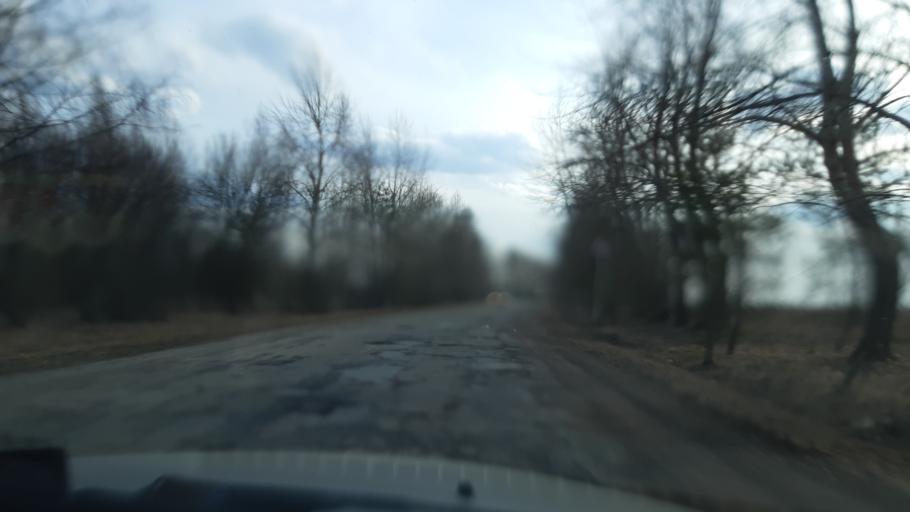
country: RU
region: Vladimir
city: Nikologory
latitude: 56.1070
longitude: 41.9814
